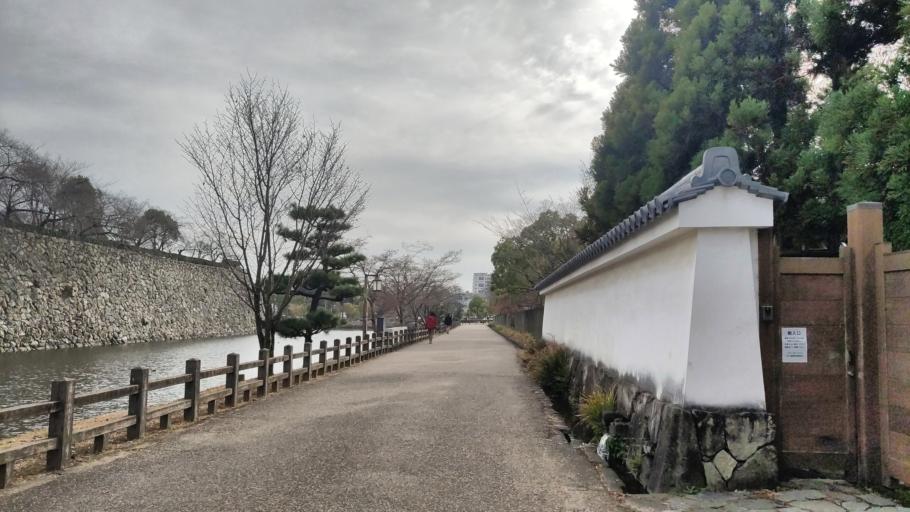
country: JP
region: Hyogo
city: Himeji
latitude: 34.8380
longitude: 134.6907
